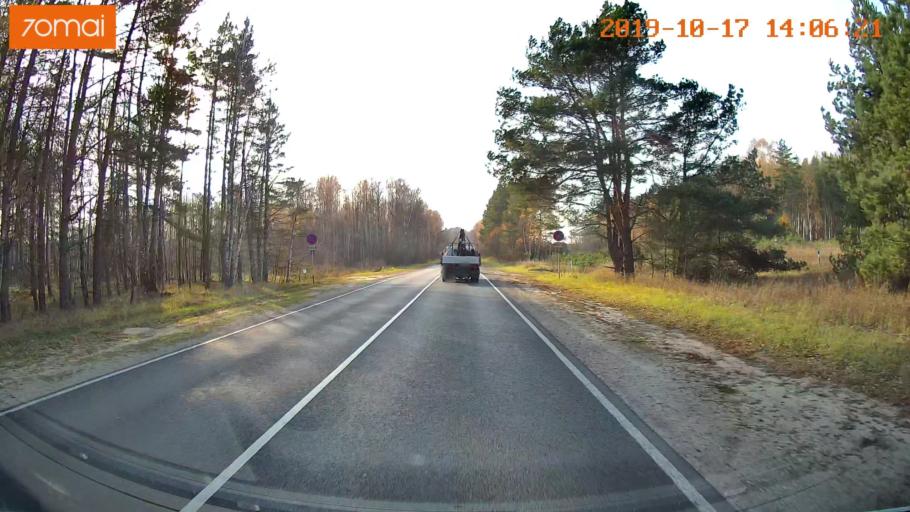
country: RU
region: Rjazan
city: Spas-Klepiki
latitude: 55.1133
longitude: 40.1077
